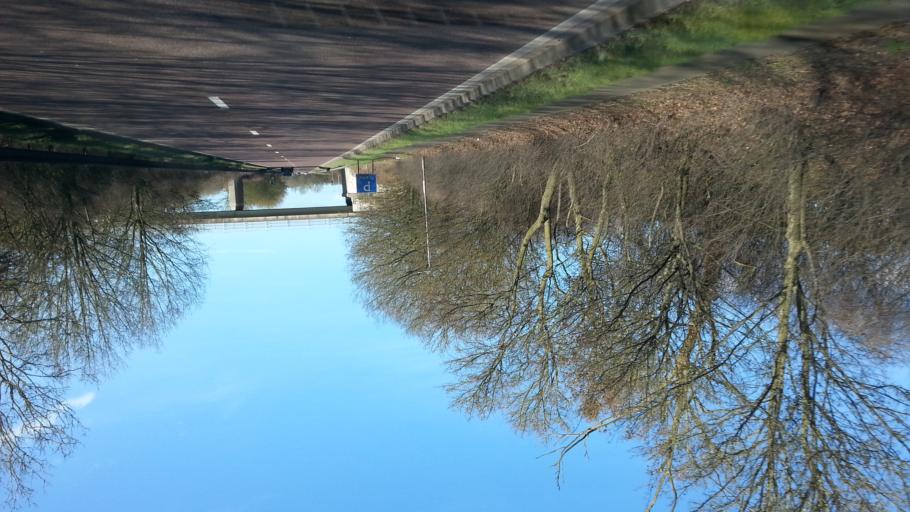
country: GB
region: England
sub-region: Solihull
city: Meriden
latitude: 52.4433
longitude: -1.6538
